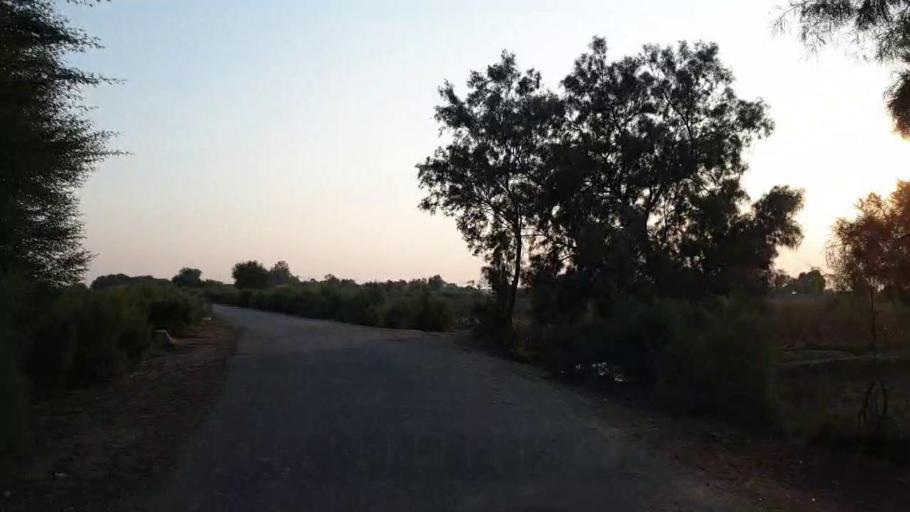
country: PK
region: Sindh
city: Sehwan
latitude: 26.4520
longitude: 67.7688
